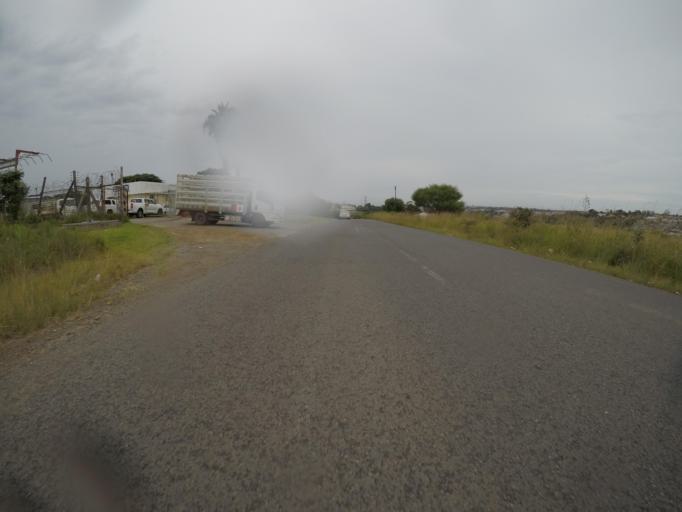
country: ZA
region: Eastern Cape
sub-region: Buffalo City Metropolitan Municipality
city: East London
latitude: -32.9864
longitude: 27.8246
